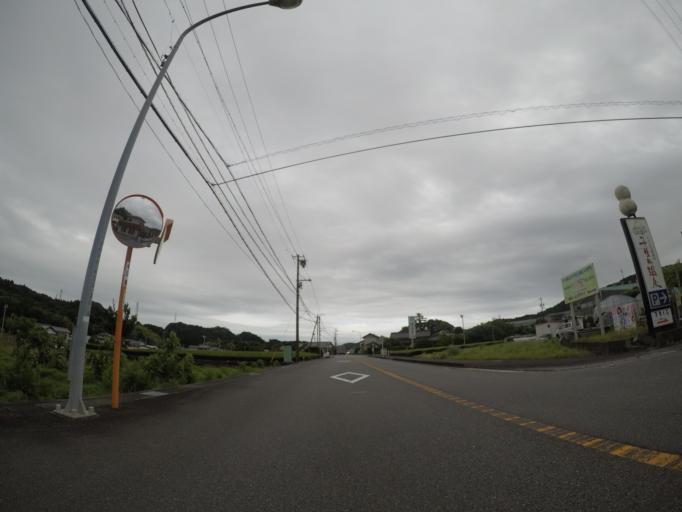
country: JP
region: Shizuoka
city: Sagara
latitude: 34.7340
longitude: 138.1610
